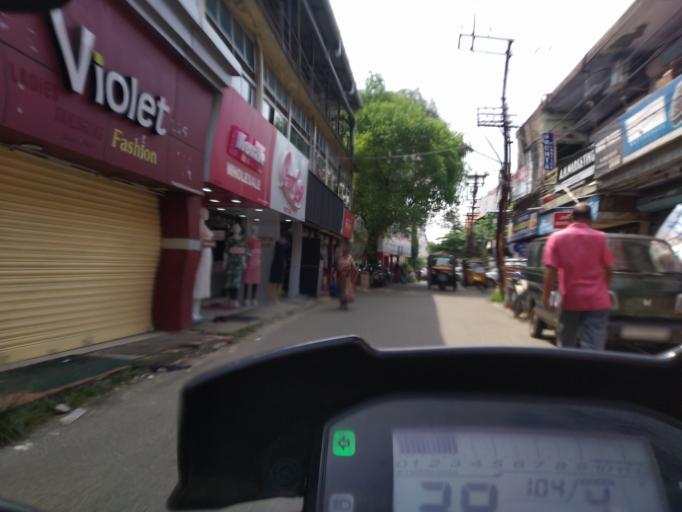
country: IN
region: Kerala
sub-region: Ernakulam
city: Cochin
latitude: 9.9768
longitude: 76.2794
